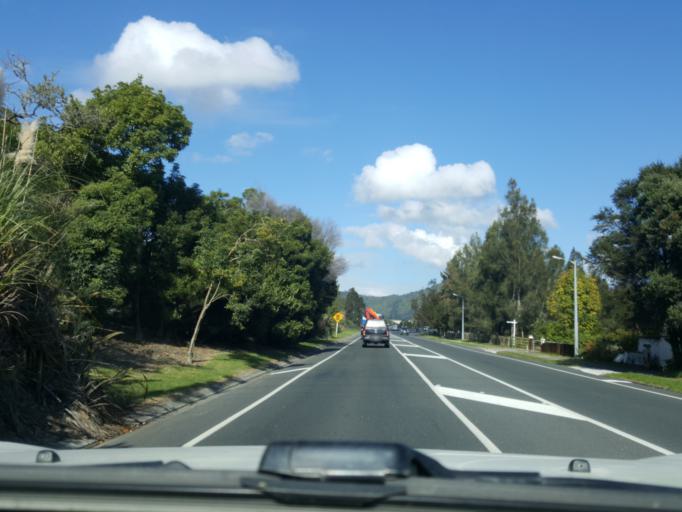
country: NZ
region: Waikato
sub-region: Waikato District
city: Ngaruawahia
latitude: -37.5748
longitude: 175.1596
